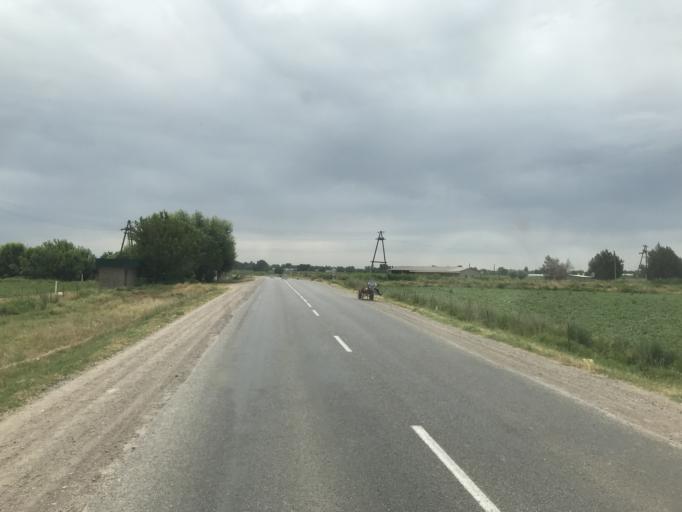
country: UZ
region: Toshkent
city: Yangiyul
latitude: 41.3352
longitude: 68.9279
